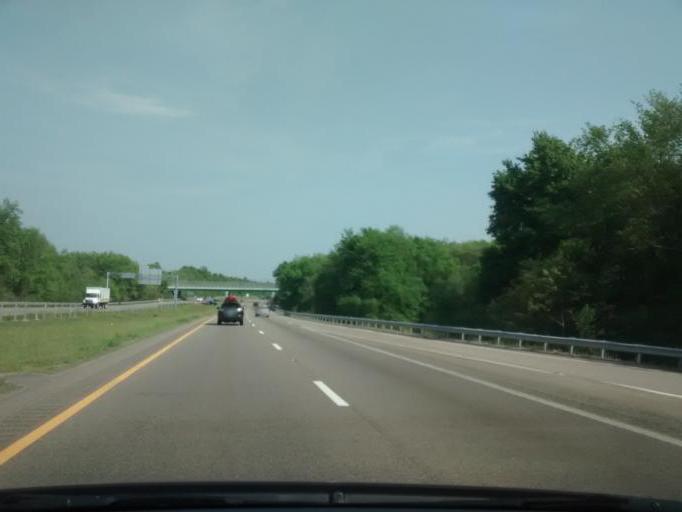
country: US
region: Massachusetts
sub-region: Plymouth County
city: Middleborough Center
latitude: 41.8702
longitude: -70.8925
